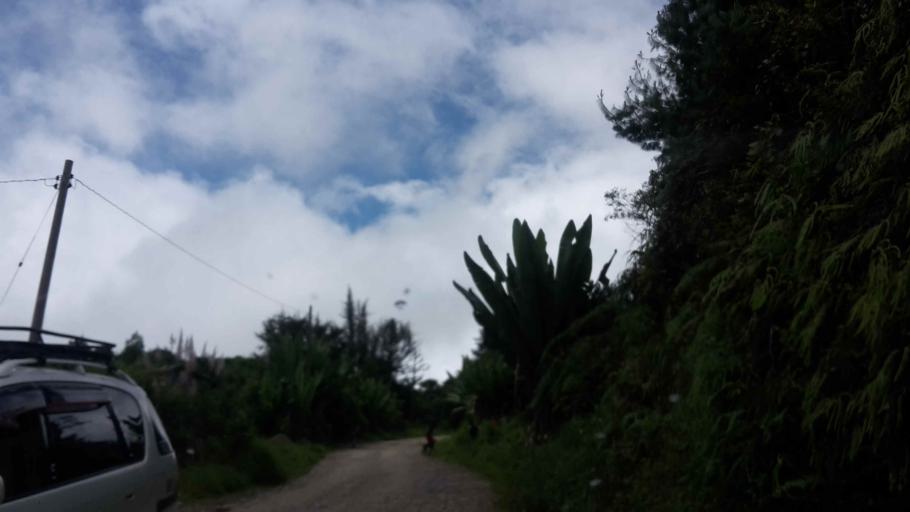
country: BO
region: Cochabamba
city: Colomi
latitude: -17.1269
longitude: -65.9362
